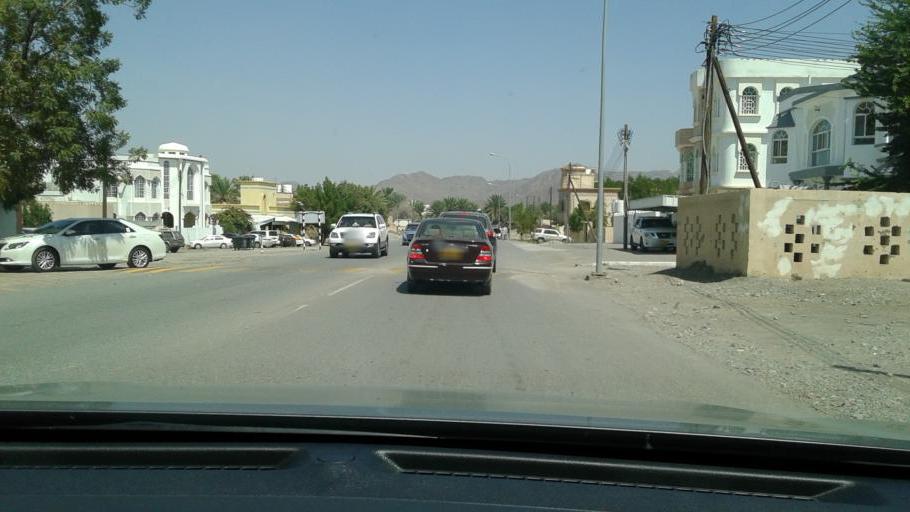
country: OM
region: Al Batinah
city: Rustaq
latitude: 23.3994
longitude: 57.4154
